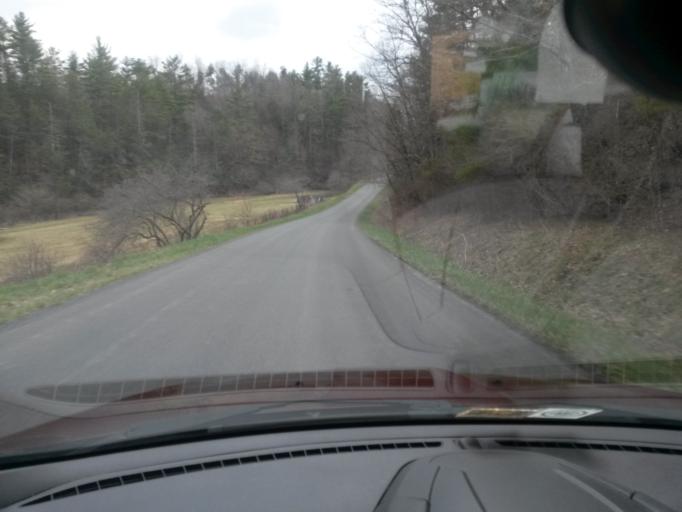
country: US
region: Virginia
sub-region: Bath County
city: Warm Springs
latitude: 38.0686
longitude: -79.8279
